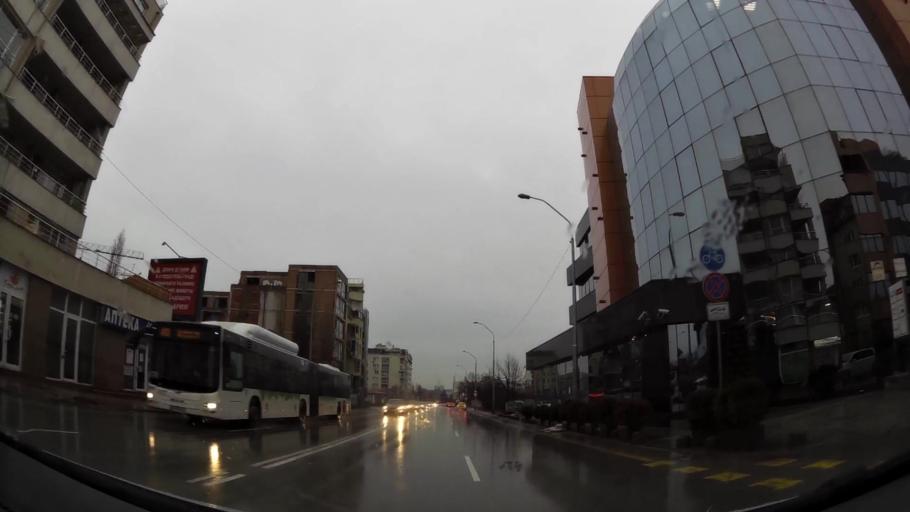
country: BG
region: Sofia-Capital
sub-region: Stolichna Obshtina
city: Sofia
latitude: 42.6571
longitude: 23.3493
